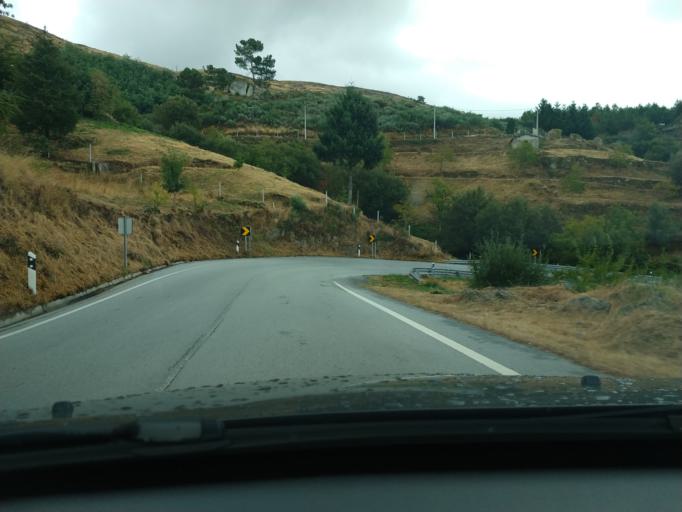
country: PT
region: Guarda
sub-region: Seia
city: Seia
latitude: 40.4137
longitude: -7.6920
